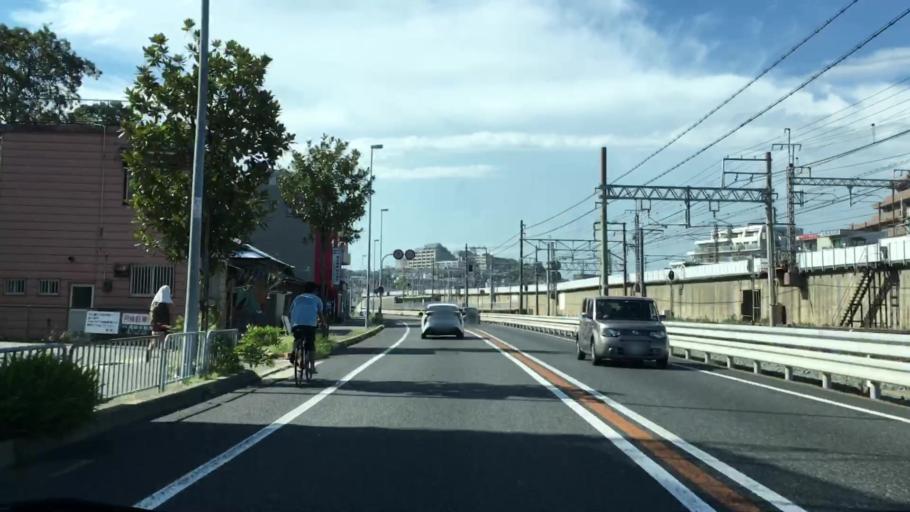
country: JP
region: Hyogo
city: Akashi
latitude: 34.6373
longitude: 135.0295
